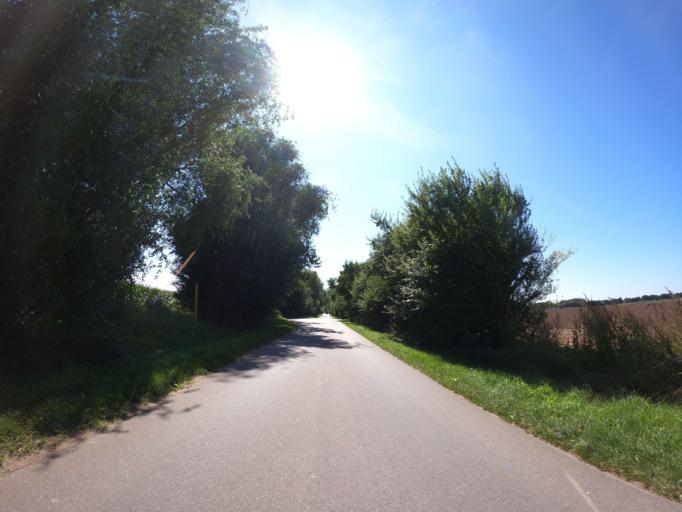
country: DE
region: Mecklenburg-Vorpommern
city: Prohn
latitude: 54.3821
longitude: 13.0247
